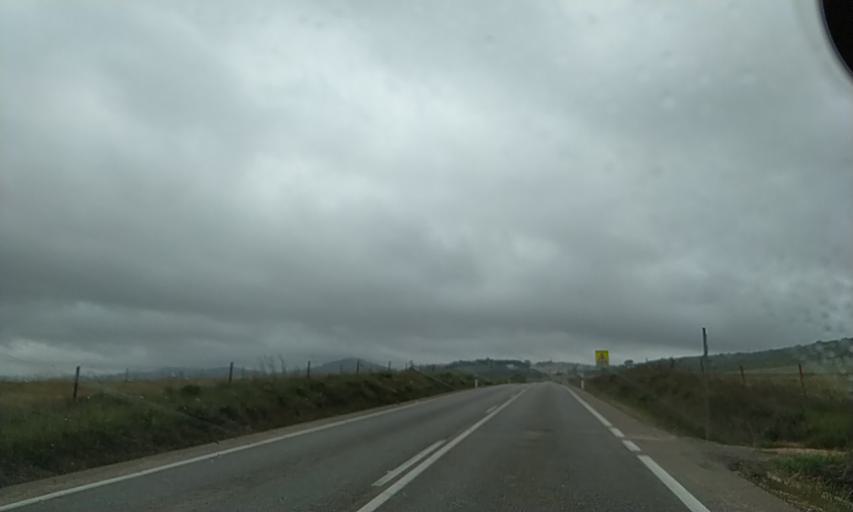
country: ES
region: Extremadura
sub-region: Provincia de Caceres
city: Caceres
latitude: 39.5011
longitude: -6.3889
